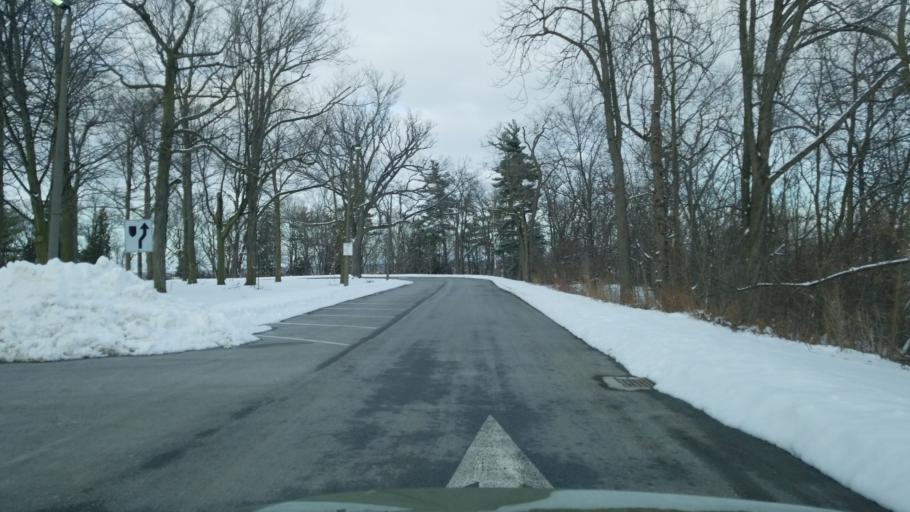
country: US
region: New York
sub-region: Niagara County
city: Lewiston
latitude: 43.1591
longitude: -79.0511
